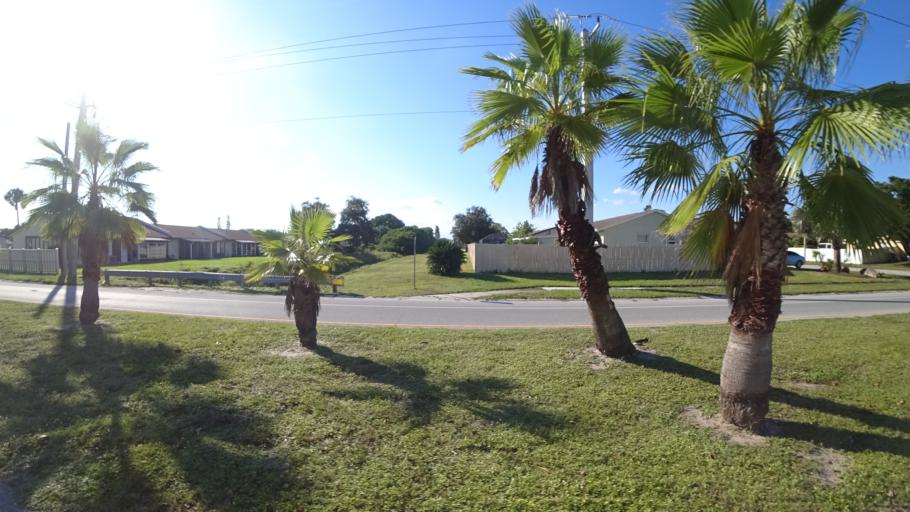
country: US
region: Florida
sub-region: Manatee County
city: South Bradenton
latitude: 27.4707
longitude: -82.5986
